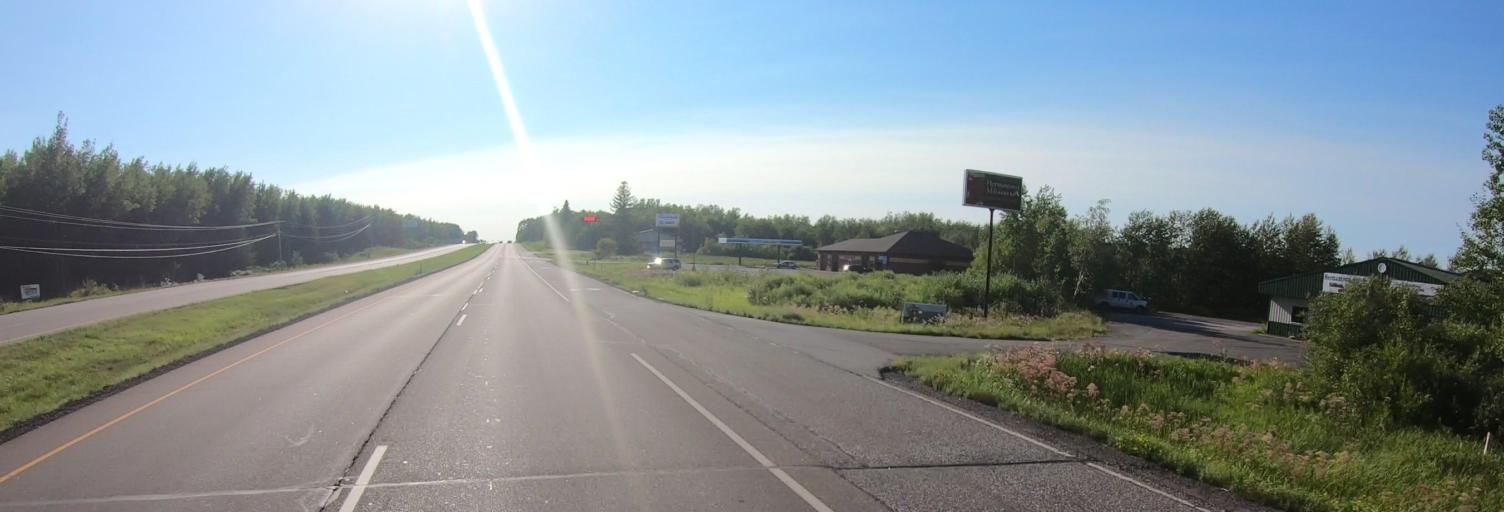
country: US
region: Minnesota
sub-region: Saint Louis County
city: Hermantown
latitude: 46.8367
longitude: -92.2228
